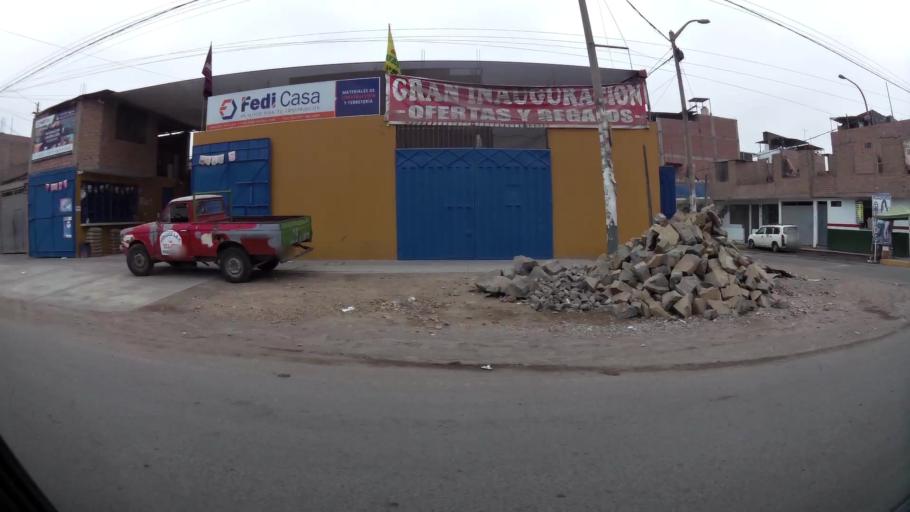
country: PE
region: Lima
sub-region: Lima
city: Independencia
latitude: -11.9688
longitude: -77.0828
